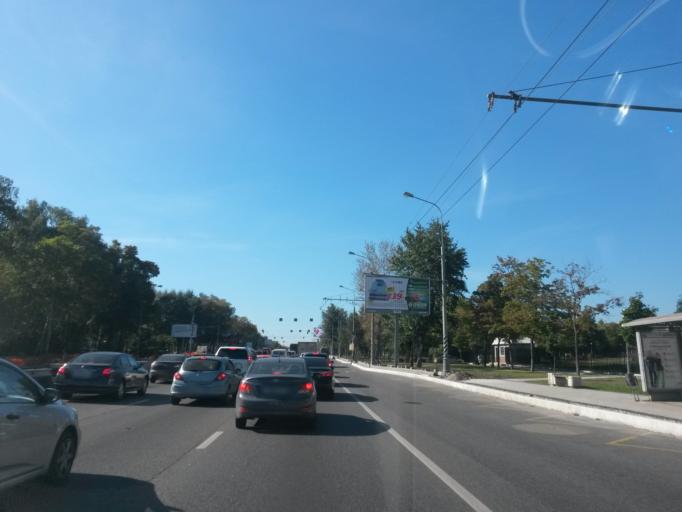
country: RU
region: Moscow
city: Nagornyy
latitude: 55.6570
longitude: 37.6449
